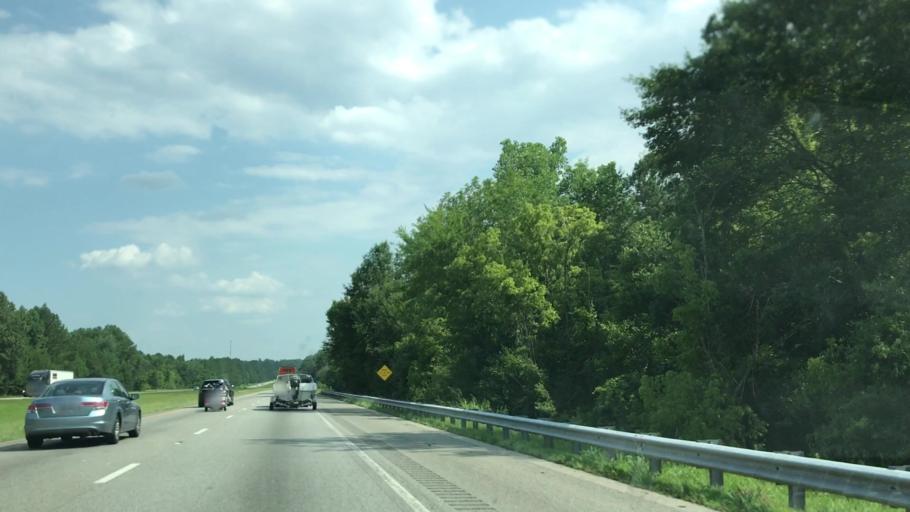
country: US
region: South Carolina
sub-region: Chester County
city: Great Falls
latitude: 34.6346
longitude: -81.0266
